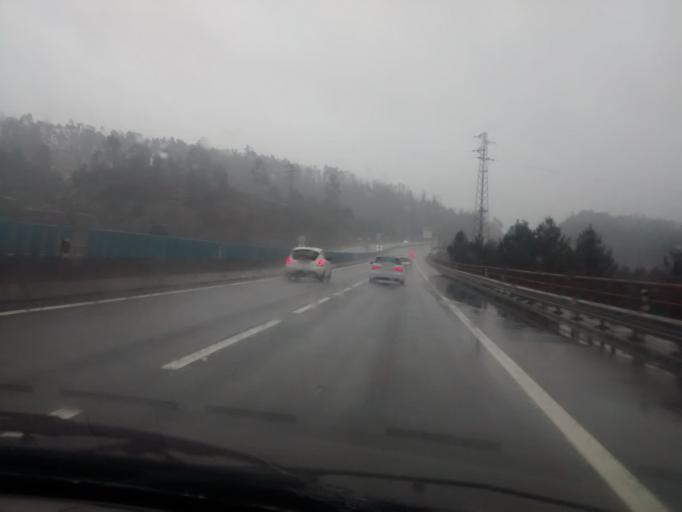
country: PT
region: Braga
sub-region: Braga
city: Braga
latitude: 41.5202
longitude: -8.4457
